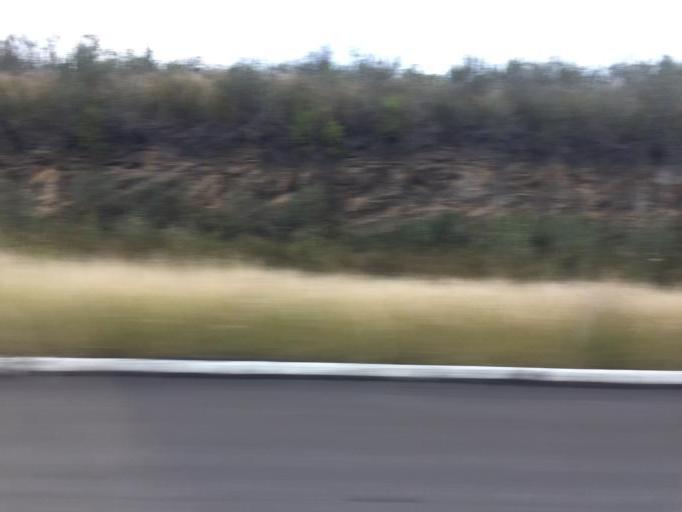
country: MX
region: Mexico
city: Huaniqueo de Morales
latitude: 19.8870
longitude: -101.5173
